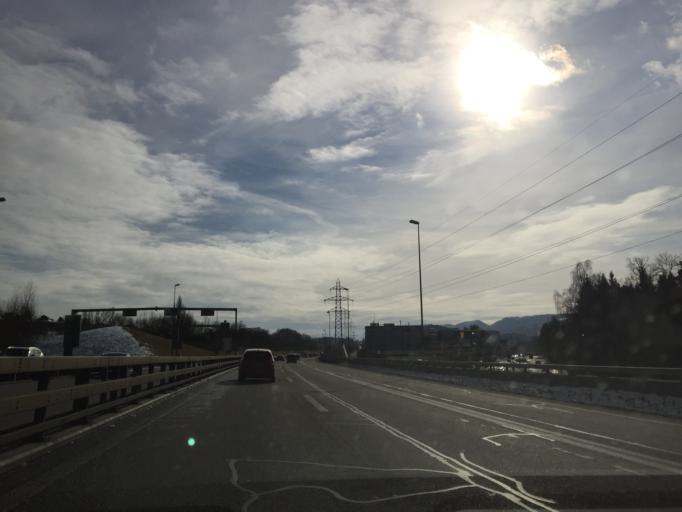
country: CH
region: Zurich
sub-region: Bezirk Horgen
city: Kilchberg / Baechler-Stocken
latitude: 47.3293
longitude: 8.5295
